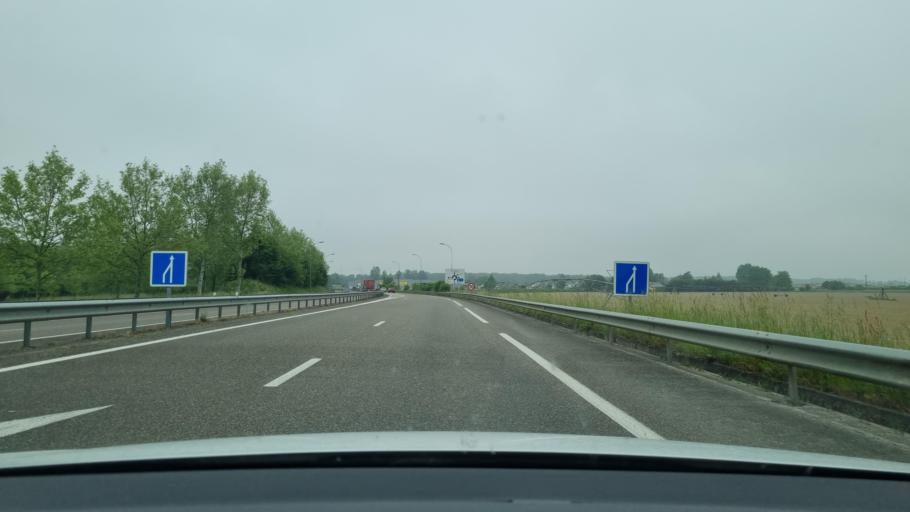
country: FR
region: Aquitaine
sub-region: Departement des Landes
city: Saint-Sever
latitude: 43.7721
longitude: -0.5576
